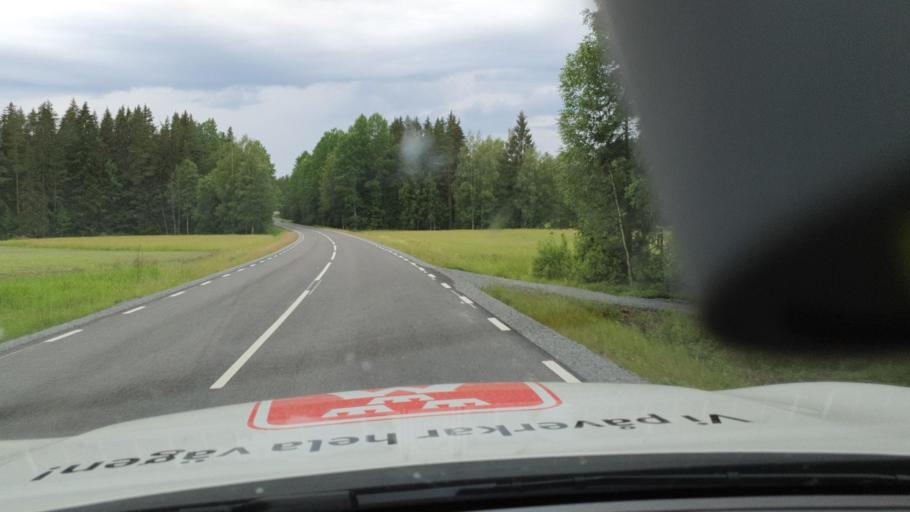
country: SE
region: OErebro
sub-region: Laxa Kommun
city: Laxa
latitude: 58.8631
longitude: 14.5409
